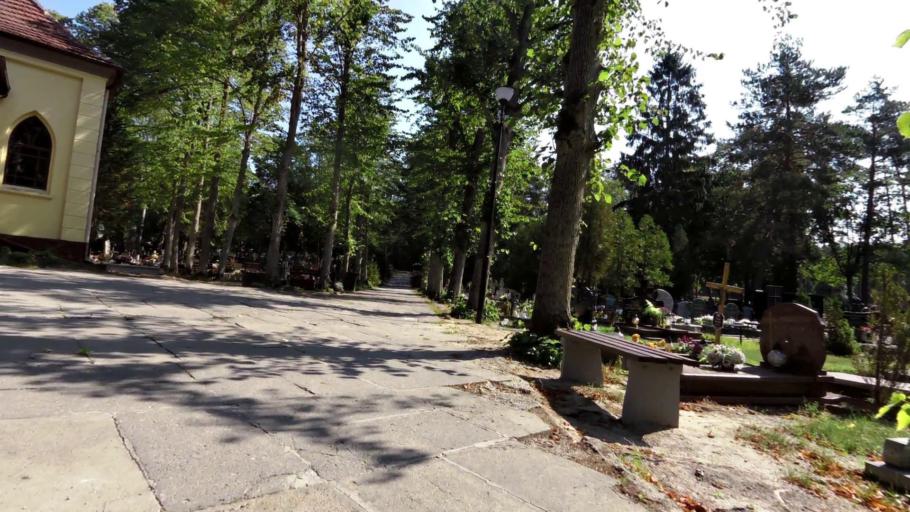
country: PL
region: West Pomeranian Voivodeship
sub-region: Powiat kamienski
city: Miedzyzdroje
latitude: 53.9240
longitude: 14.4632
